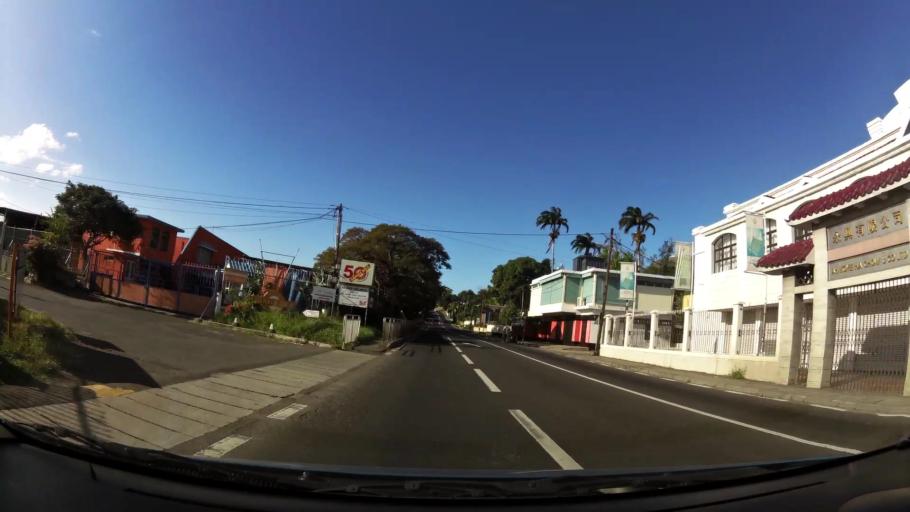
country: MU
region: Moka
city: Pailles
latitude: -20.1731
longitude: 57.4755
